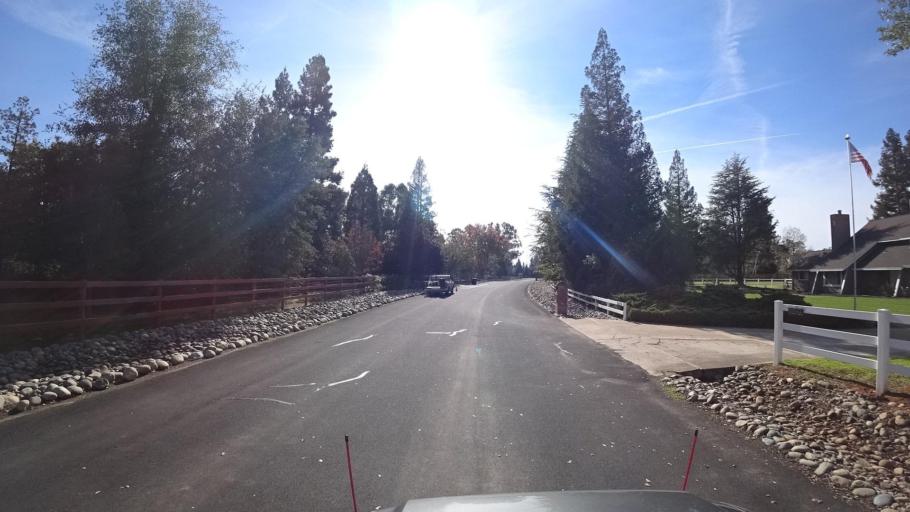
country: US
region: California
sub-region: Sacramento County
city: Wilton
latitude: 38.4380
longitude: -121.2875
